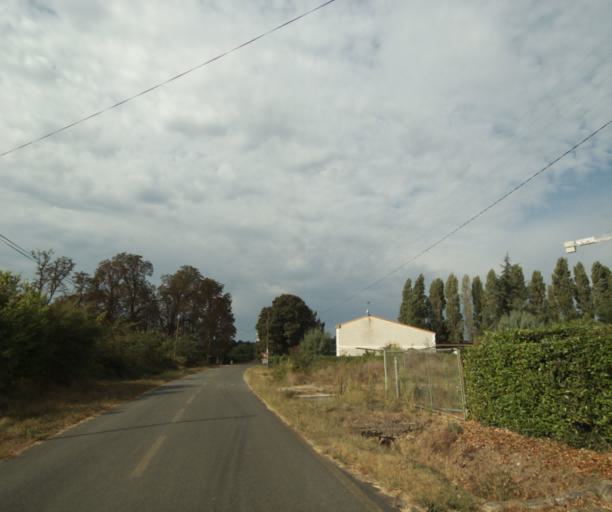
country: FR
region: Poitou-Charentes
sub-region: Departement de la Charente-Maritime
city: Tonnay-Charente
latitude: 45.9529
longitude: -0.8699
